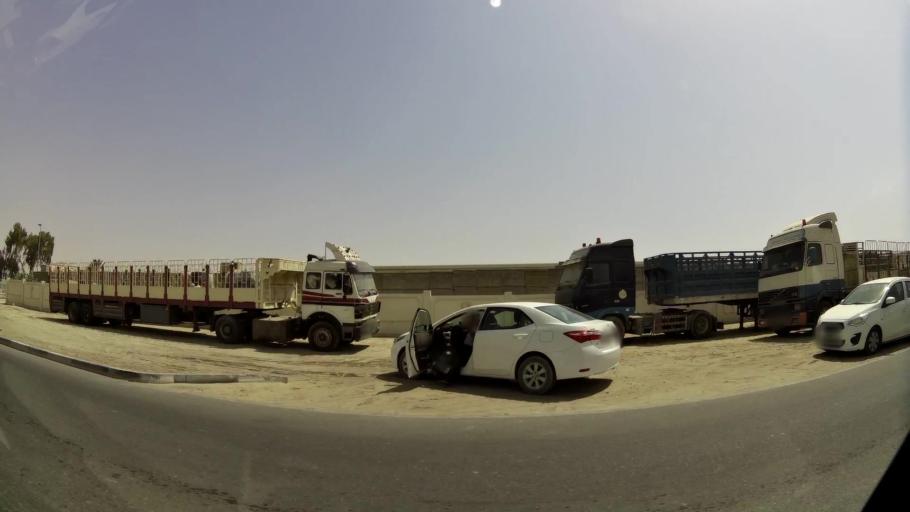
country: AE
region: Dubai
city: Dubai
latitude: 25.1483
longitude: 55.2406
